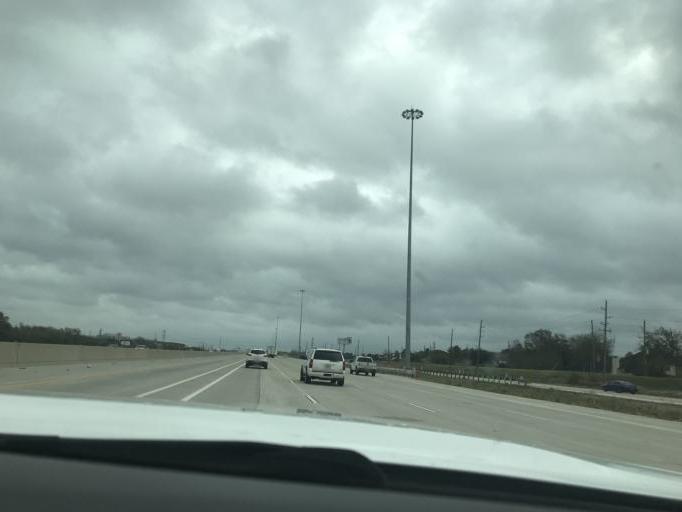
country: US
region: Texas
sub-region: Fort Bend County
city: Greatwood
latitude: 29.5586
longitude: -95.7033
